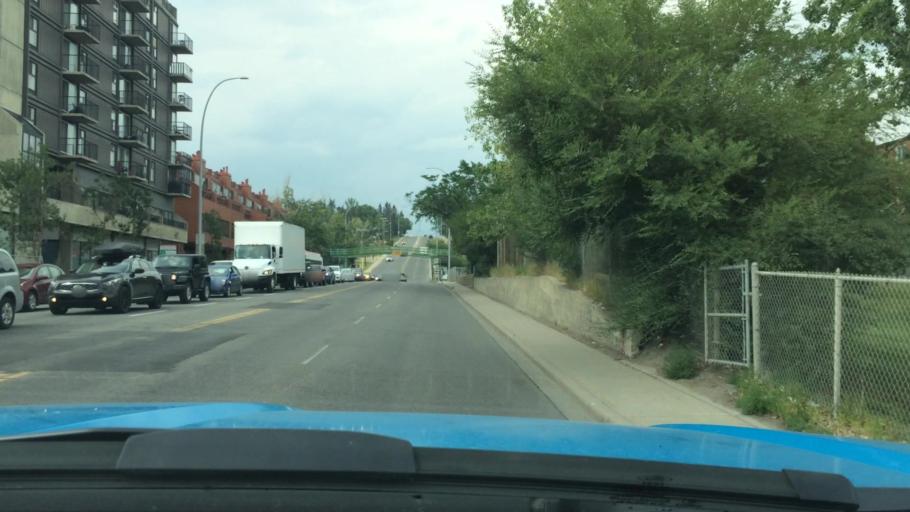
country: CA
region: Alberta
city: Calgary
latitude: 51.0580
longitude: -114.0947
